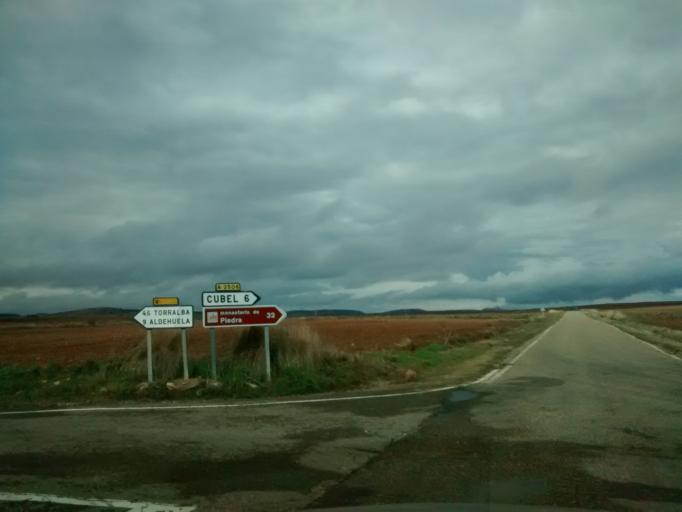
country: ES
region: Aragon
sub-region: Provincia de Zaragoza
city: Torralba de los Frailes
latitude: 41.0509
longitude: -1.6139
